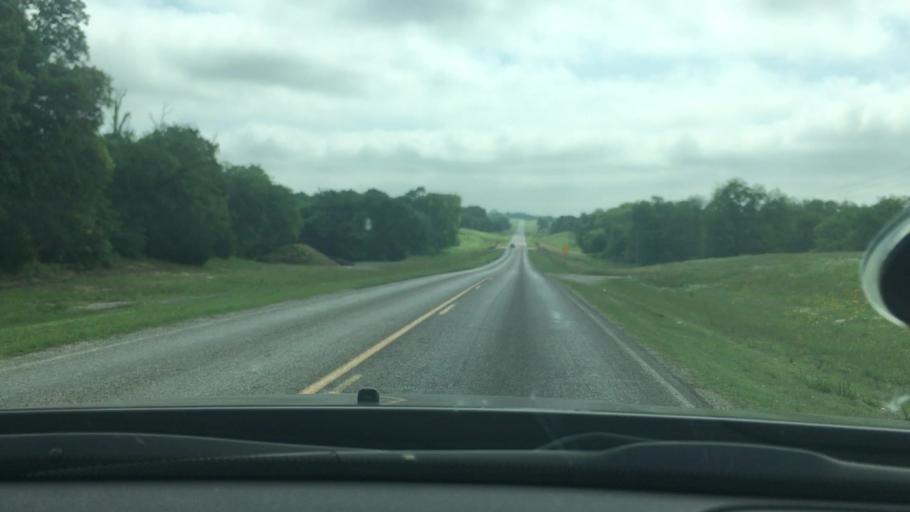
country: US
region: Oklahoma
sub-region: Johnston County
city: Tishomingo
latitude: 34.2303
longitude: -96.6488
